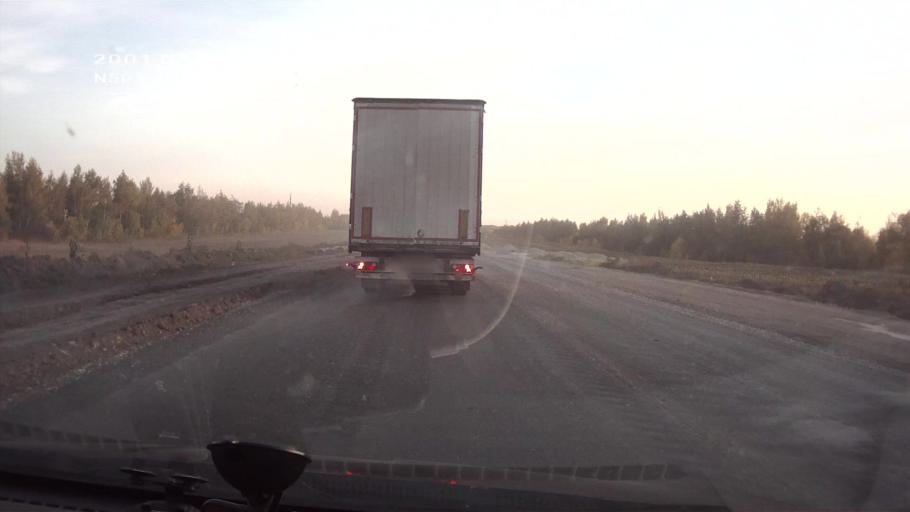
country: RU
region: Saratov
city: Kamenskiy
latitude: 50.9271
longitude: 45.5993
